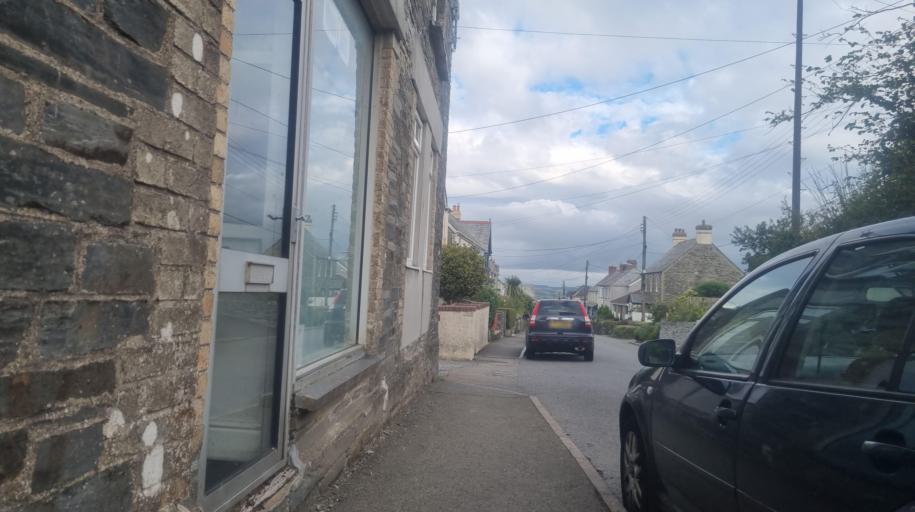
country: GB
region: England
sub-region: Cornwall
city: Tintagel
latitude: 50.6231
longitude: -4.7316
